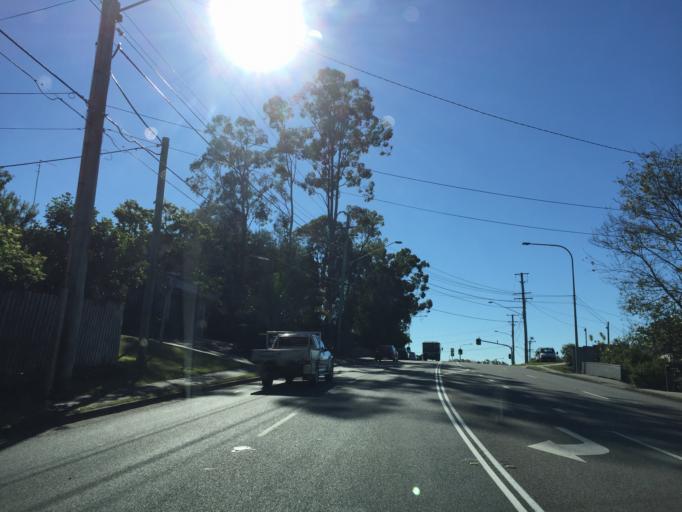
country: AU
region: Queensland
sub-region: Brisbane
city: Everton Park
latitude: -27.4126
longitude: 152.9616
